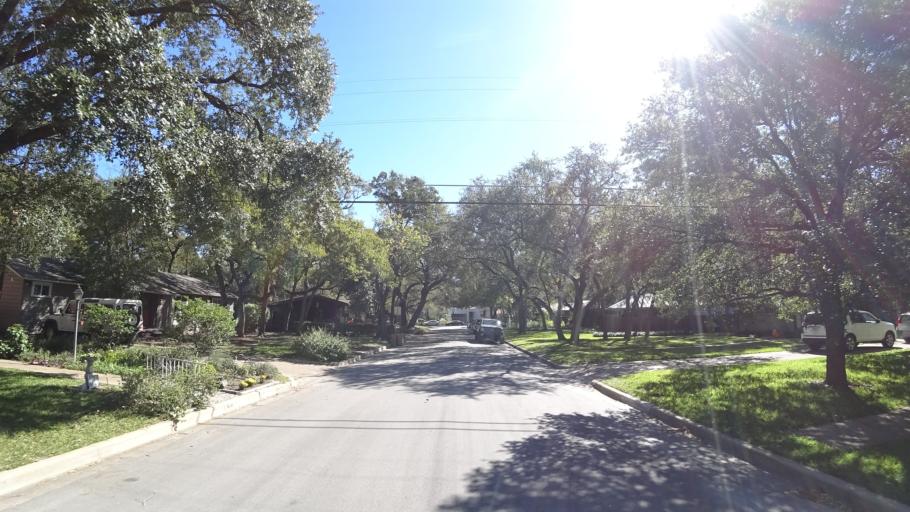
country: US
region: Texas
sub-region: Travis County
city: Austin
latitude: 30.3242
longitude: -97.7473
